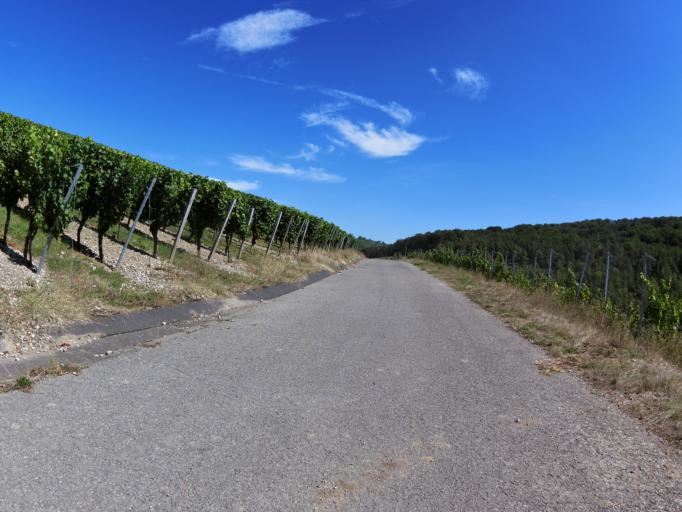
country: DE
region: Bavaria
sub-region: Regierungsbezirk Unterfranken
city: Thungersheim
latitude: 49.8669
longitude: 9.8607
